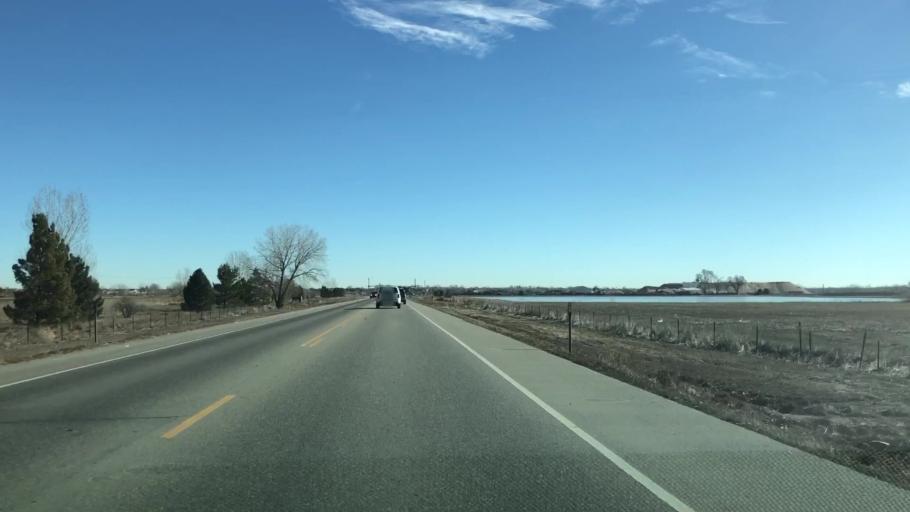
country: US
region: Colorado
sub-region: Weld County
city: Windsor
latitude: 40.4792
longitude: -104.9511
